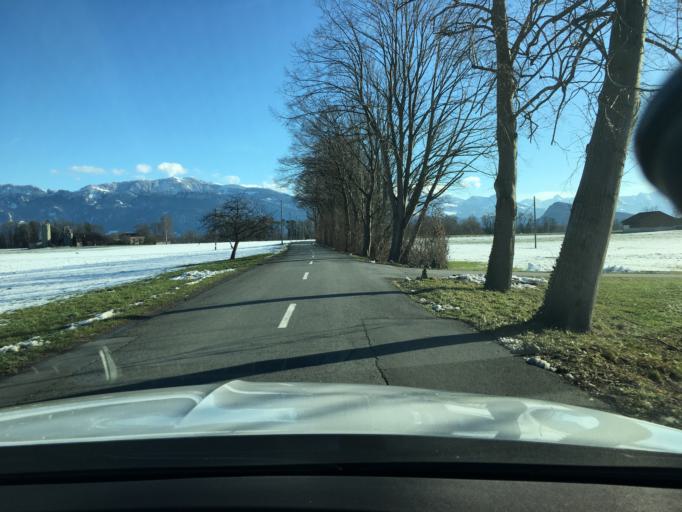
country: CH
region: Saint Gallen
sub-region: Wahlkreis Rheintal
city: Rebstein
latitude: 47.3837
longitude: 9.5826
